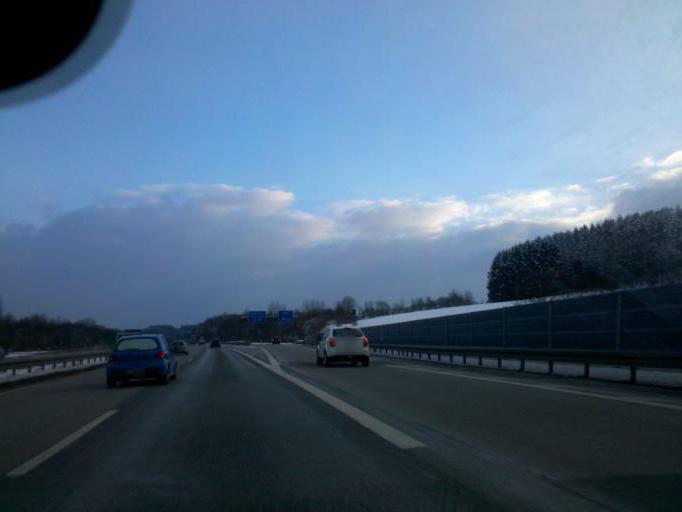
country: DE
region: North Rhine-Westphalia
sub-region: Regierungsbezirk Arnsberg
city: Olpe
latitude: 50.9924
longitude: 7.8342
